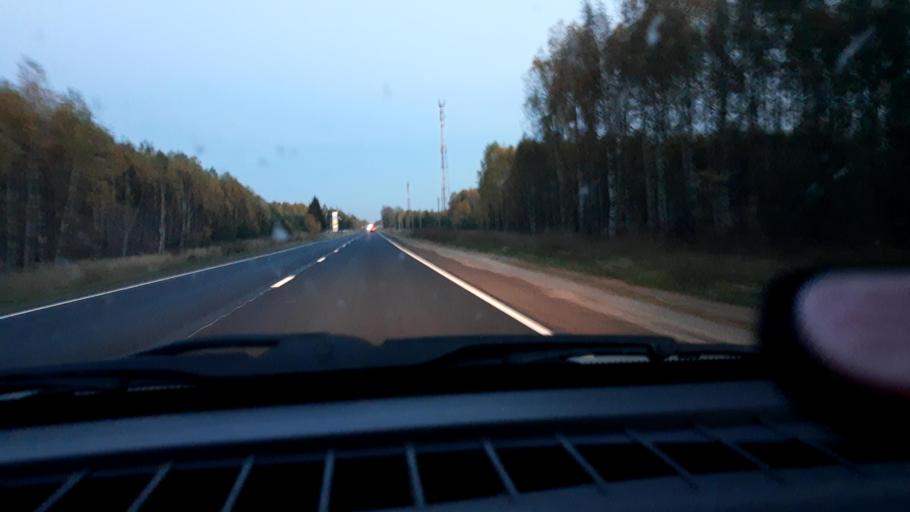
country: RU
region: Nizjnij Novgorod
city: Novaya Balakhna
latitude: 56.6019
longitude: 43.6291
